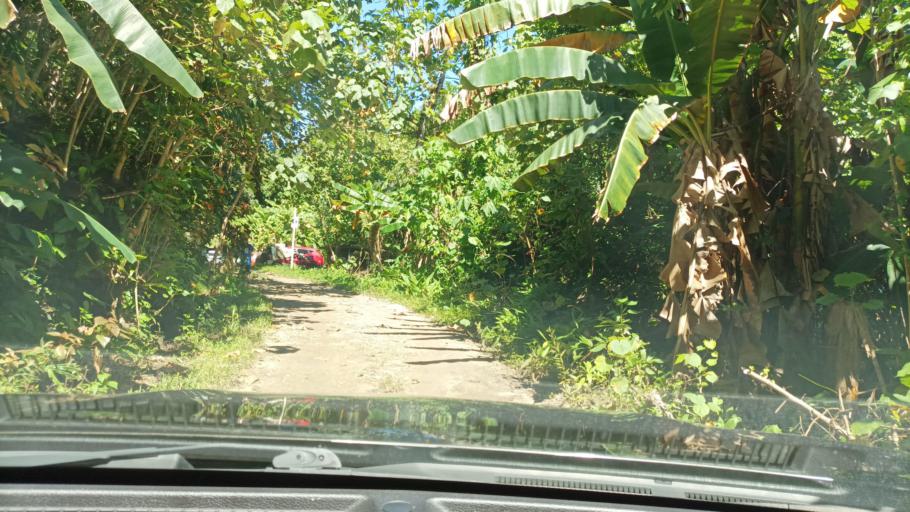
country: FM
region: Pohnpei
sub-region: Madolenihm Municipality
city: Madolenihm Municipality Government
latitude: 6.8430
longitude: 158.3201
